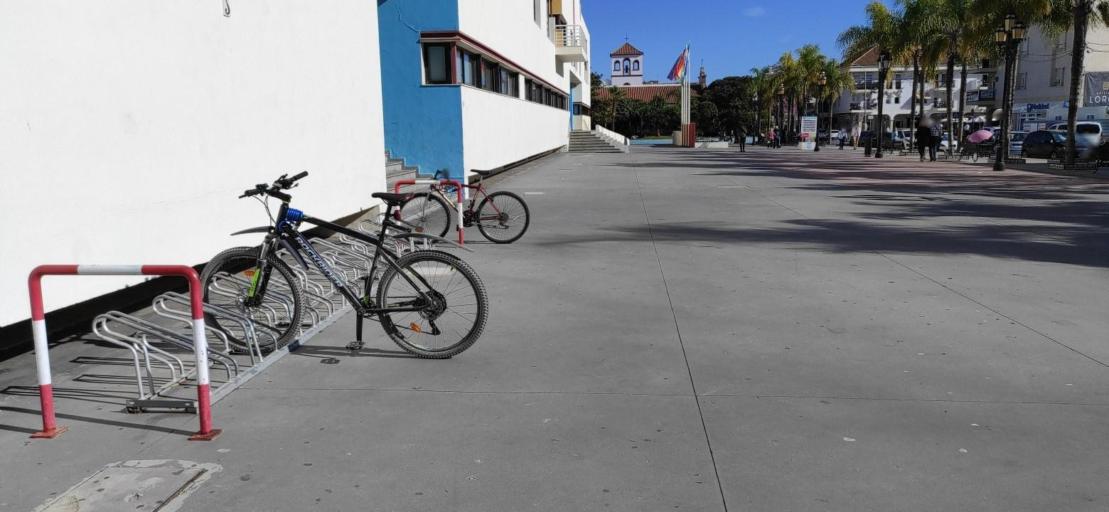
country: ES
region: Andalusia
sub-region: Provincia de Malaga
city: Torremolinos
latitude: 36.6210
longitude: -4.5078
